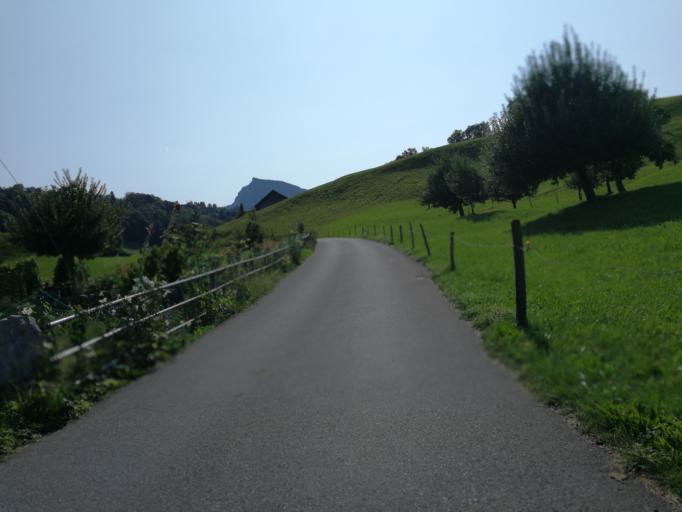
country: CH
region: Saint Gallen
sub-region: Wahlkreis Toggenburg
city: Krummenau
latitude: 47.2435
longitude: 9.1719
